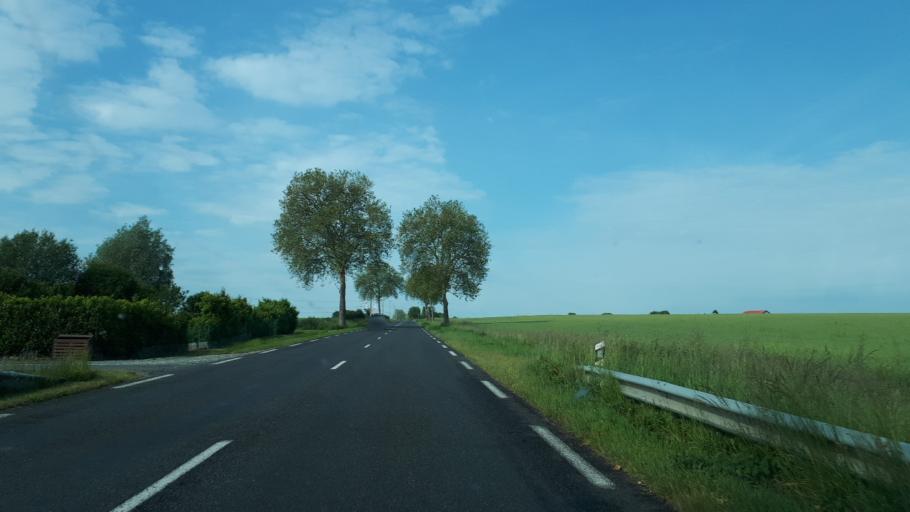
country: FR
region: Centre
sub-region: Departement d'Indre-et-Loire
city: Villedomer
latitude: 47.5641
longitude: 0.8819
